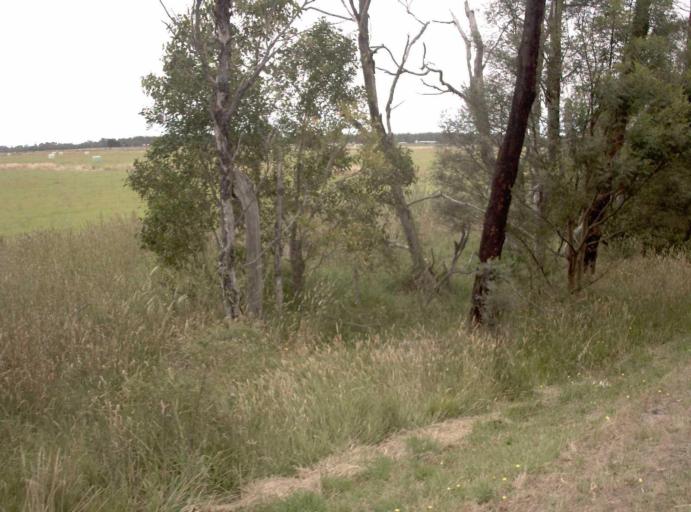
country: AU
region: Victoria
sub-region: Latrobe
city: Traralgon
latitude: -38.4852
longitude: 146.8203
